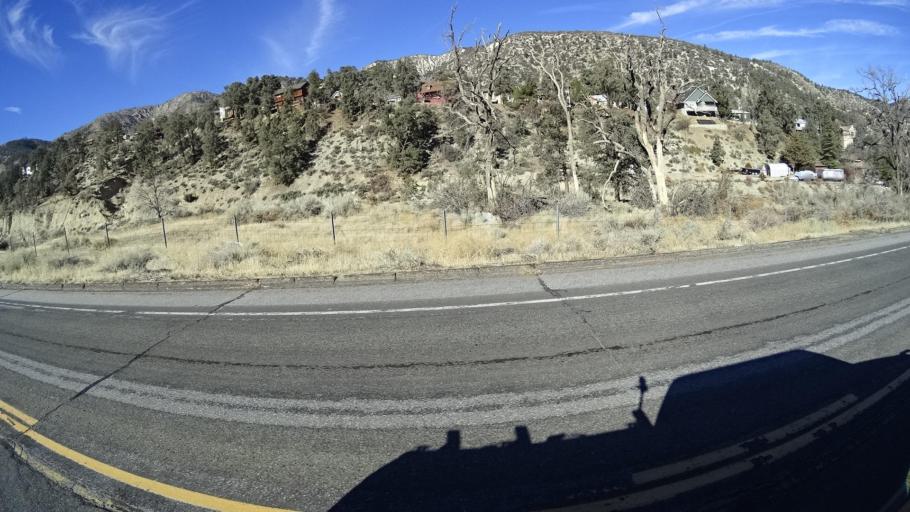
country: US
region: California
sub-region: Kern County
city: Frazier Park
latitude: 34.8207
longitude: -118.9510
